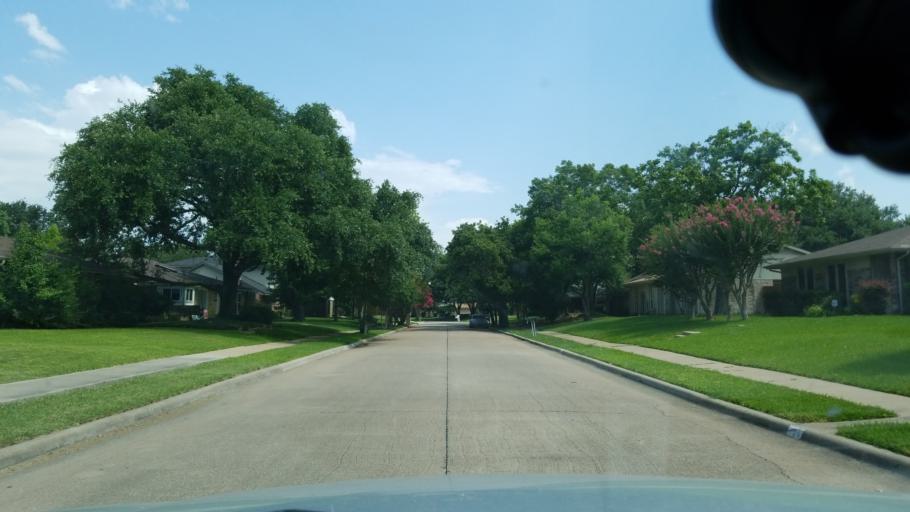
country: US
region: Texas
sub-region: Dallas County
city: Coppell
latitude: 32.9662
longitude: -96.9901
